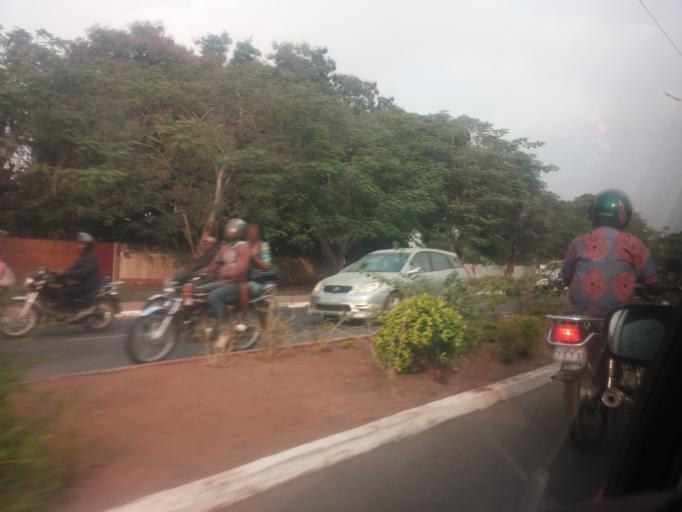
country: TG
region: Maritime
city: Lome
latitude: 6.1565
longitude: 1.2271
